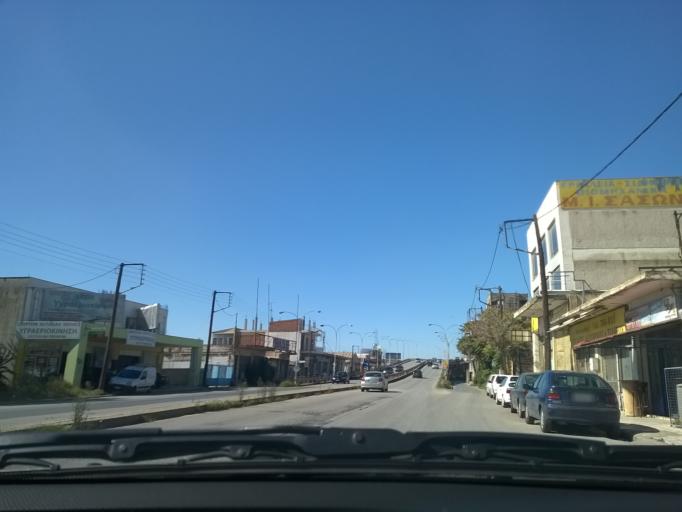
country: GR
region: Central Macedonia
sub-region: Nomos Thessalonikis
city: Menemeni
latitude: 40.6601
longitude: 22.9002
